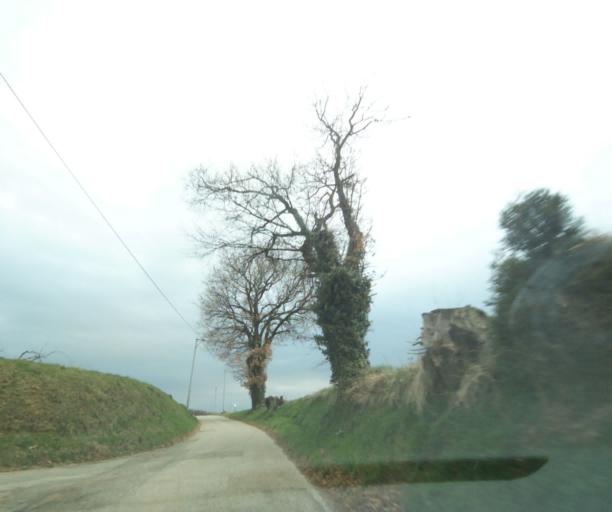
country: FR
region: Rhone-Alpes
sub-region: Departement de la Drome
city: Bourg-les-Valence
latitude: 44.9848
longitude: 4.9149
